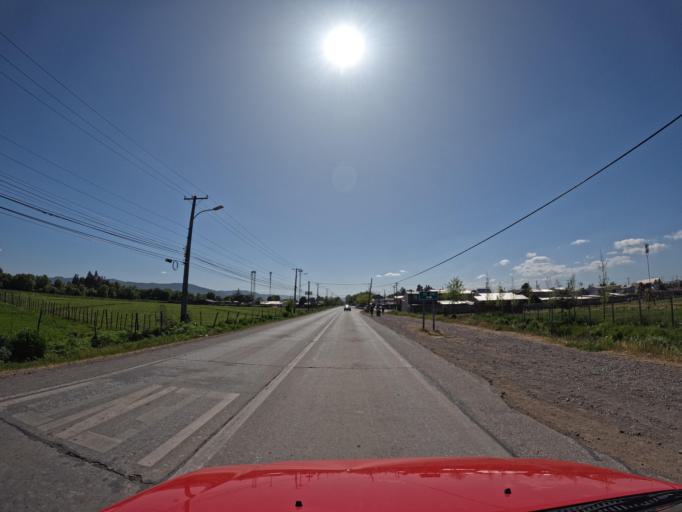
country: CL
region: Maule
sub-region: Provincia de Curico
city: Molina
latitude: -35.0621
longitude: -71.2604
